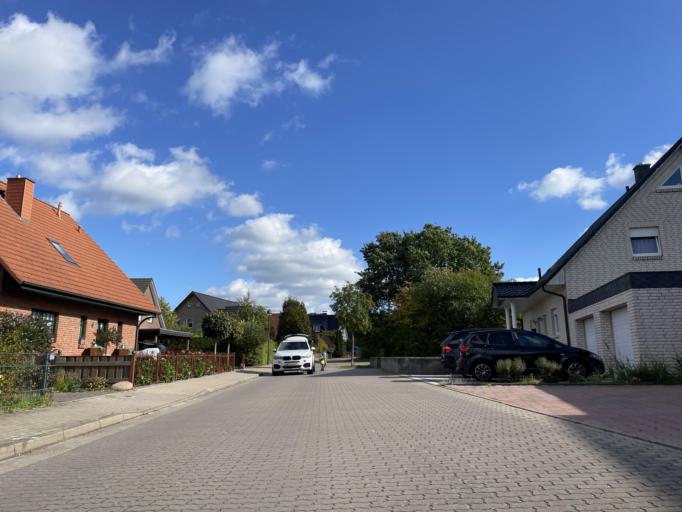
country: DE
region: Lower Saxony
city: Barendorf
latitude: 53.2341
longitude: 10.5215
